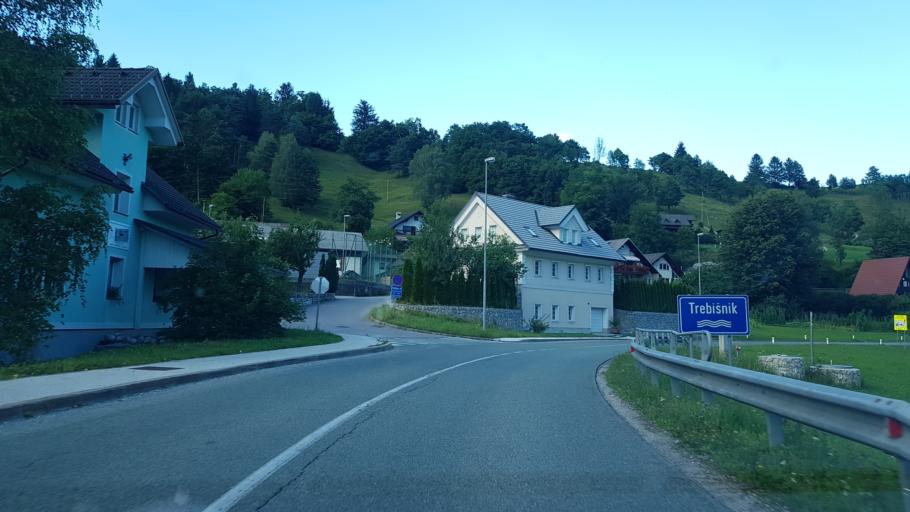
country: SI
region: Gorenja Vas-Poljane
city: Gorenja Vas
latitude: 46.0962
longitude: 14.1010
